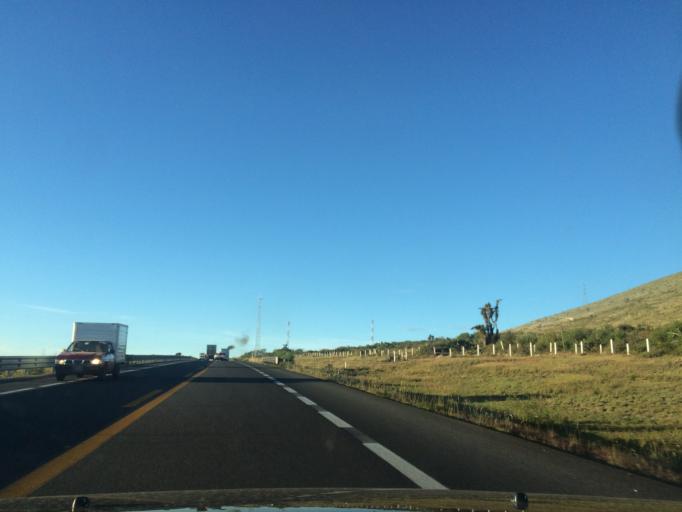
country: MX
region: Puebla
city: Morelos Canada
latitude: 18.7202
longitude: -97.4724
